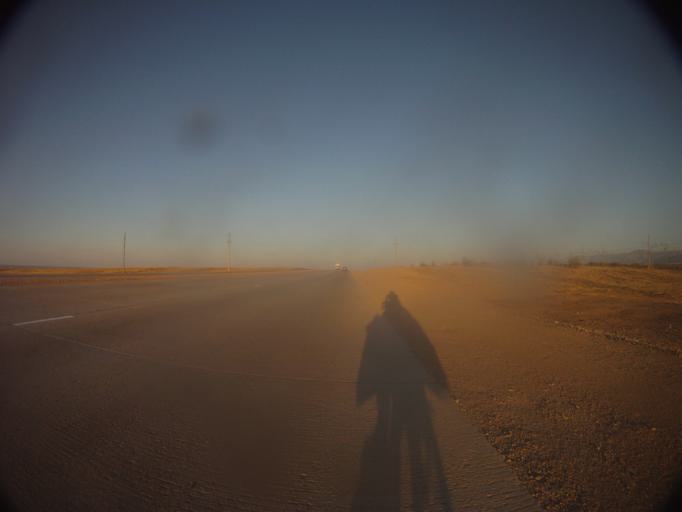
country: KZ
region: Zhambyl
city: Sarykemer
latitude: 43.0038
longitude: 71.6351
